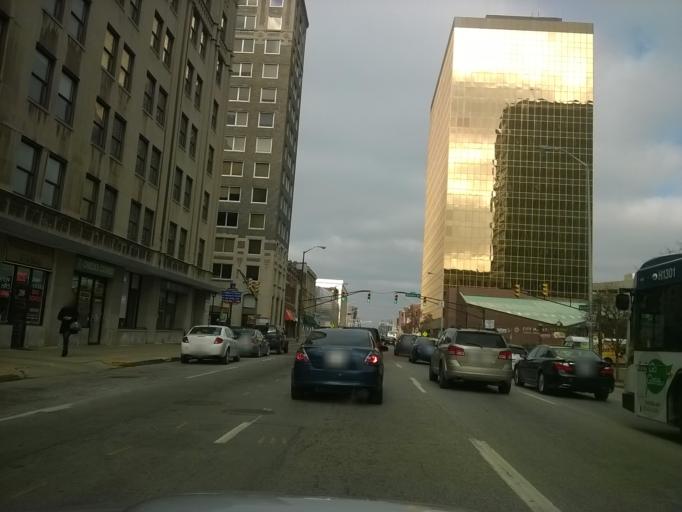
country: US
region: Indiana
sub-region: Marion County
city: Indianapolis
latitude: 39.7679
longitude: -86.1545
